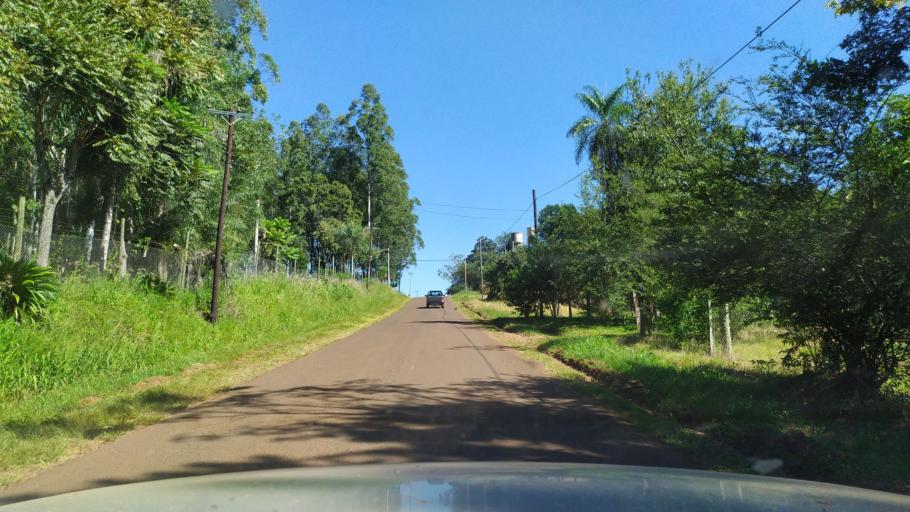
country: AR
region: Misiones
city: Caraguatay
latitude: -26.6486
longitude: -54.7469
